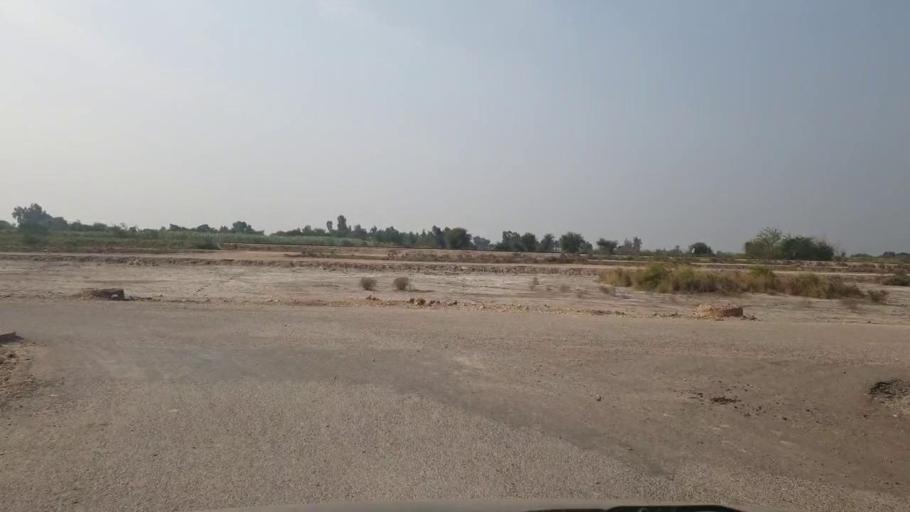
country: PK
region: Sindh
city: Tando Muhammad Khan
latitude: 25.1334
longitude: 68.5195
